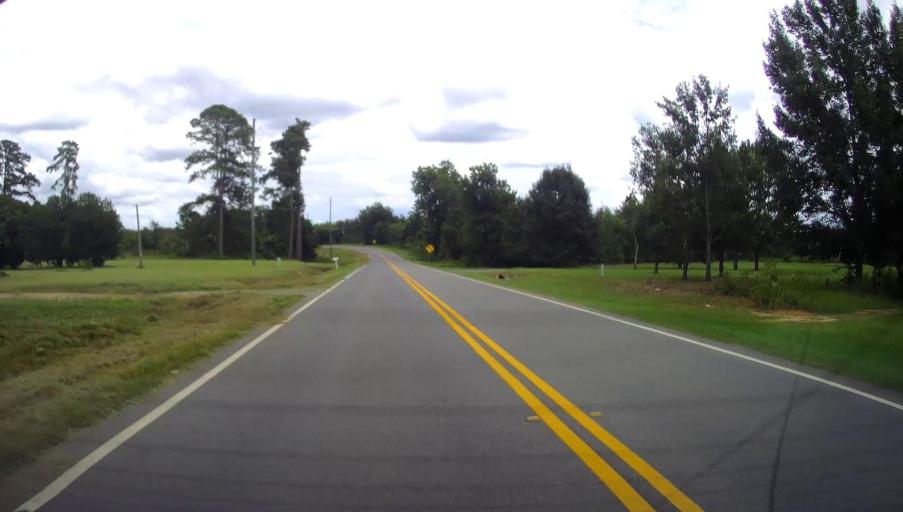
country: US
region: Georgia
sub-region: Macon County
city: Oglethorpe
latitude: 32.2649
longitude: -84.1010
